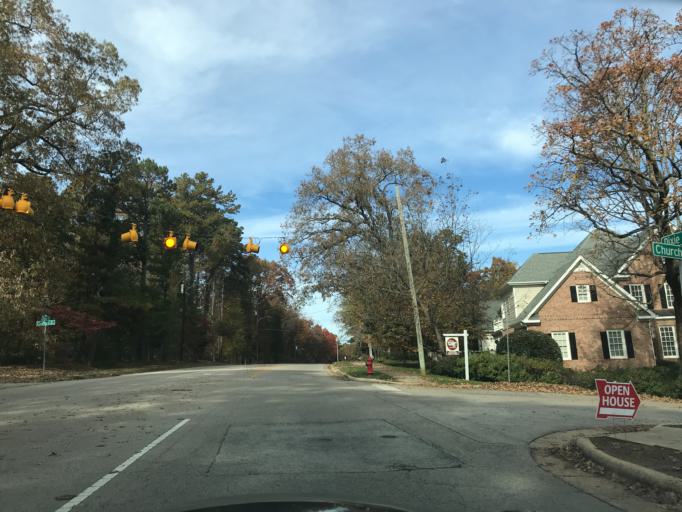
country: US
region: North Carolina
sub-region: Wake County
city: West Raleigh
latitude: 35.8059
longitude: -78.6780
